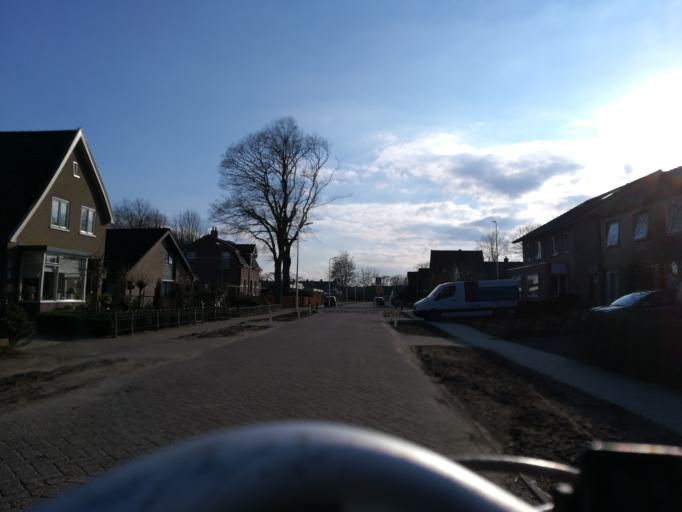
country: NL
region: Gelderland
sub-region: Gemeente Epe
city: Epe
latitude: 52.3453
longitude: 5.9761
